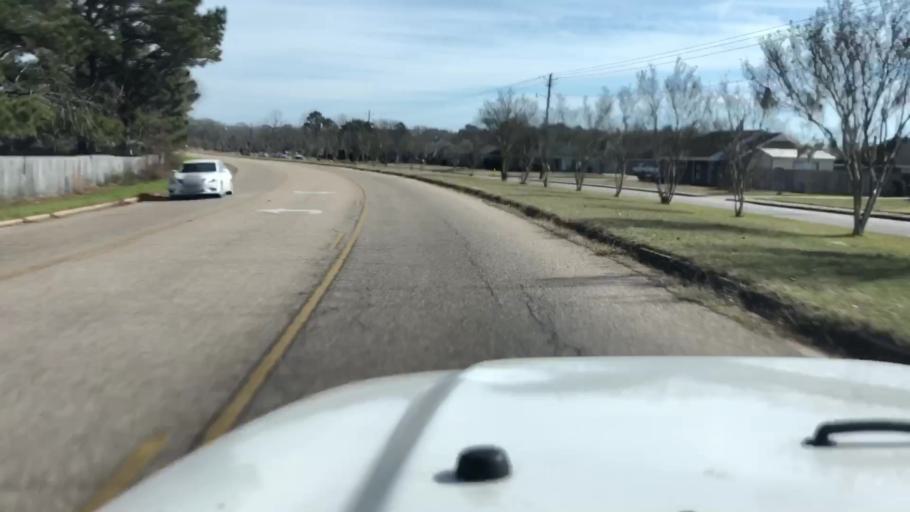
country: US
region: Alabama
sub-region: Elmore County
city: Blue Ridge
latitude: 32.4043
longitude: -86.1772
